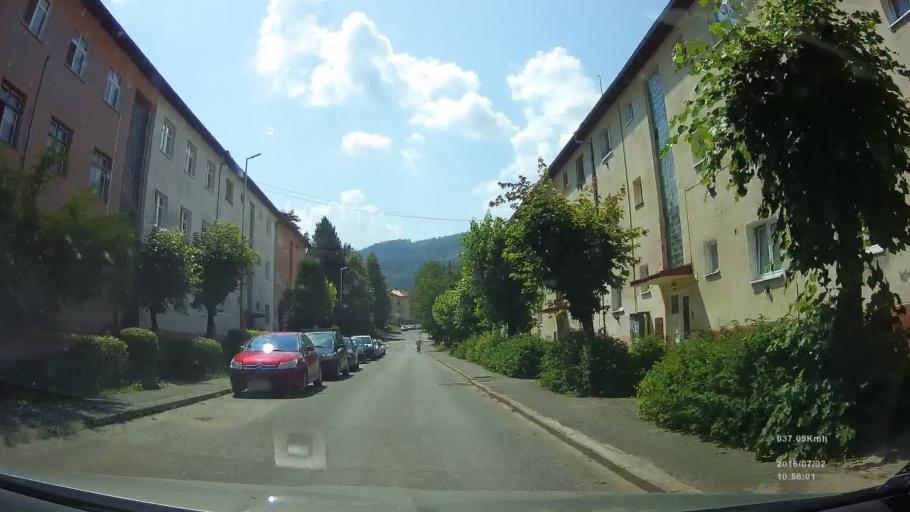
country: SK
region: Kosicky
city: Krompachy
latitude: 48.9159
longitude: 20.8754
